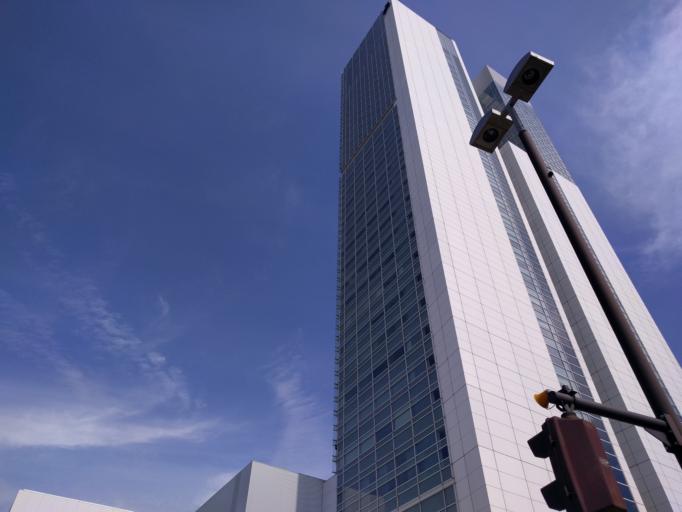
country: JP
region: Niigata
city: Niigata-shi
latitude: 37.9246
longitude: 139.0599
